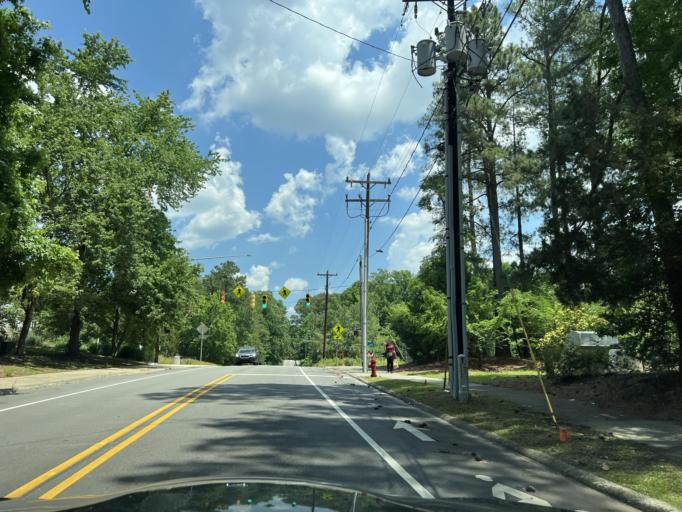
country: US
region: North Carolina
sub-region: Durham County
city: Durham
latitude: 36.0289
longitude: -78.8999
